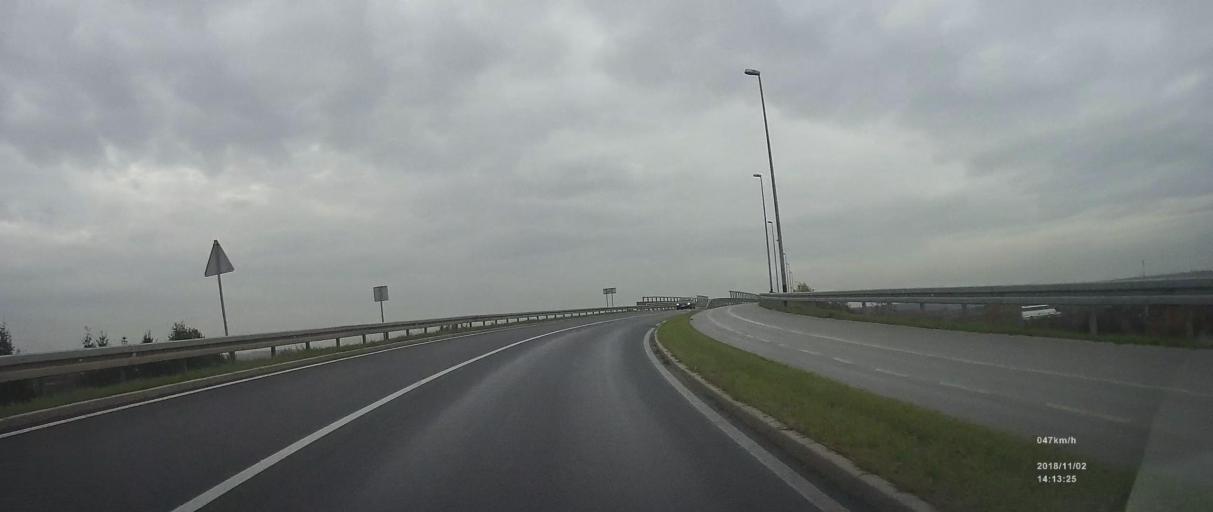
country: HR
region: Zagrebacka
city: Gradici
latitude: 45.6990
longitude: 16.0620
